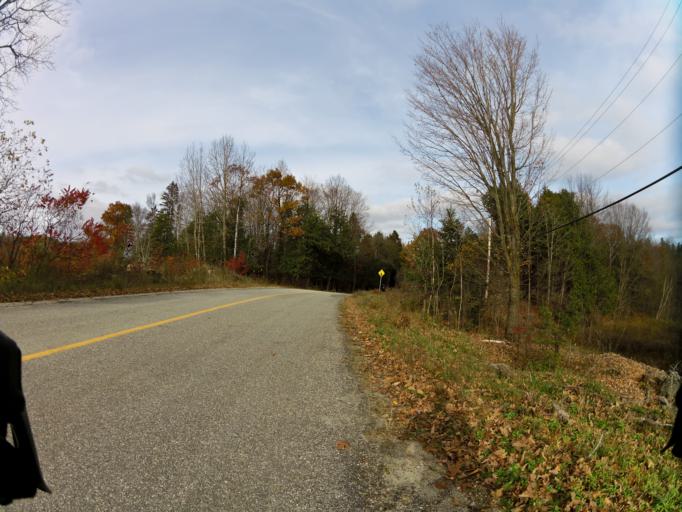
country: CA
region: Quebec
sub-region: Outaouais
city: Wakefield
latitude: 45.7380
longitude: -75.9738
